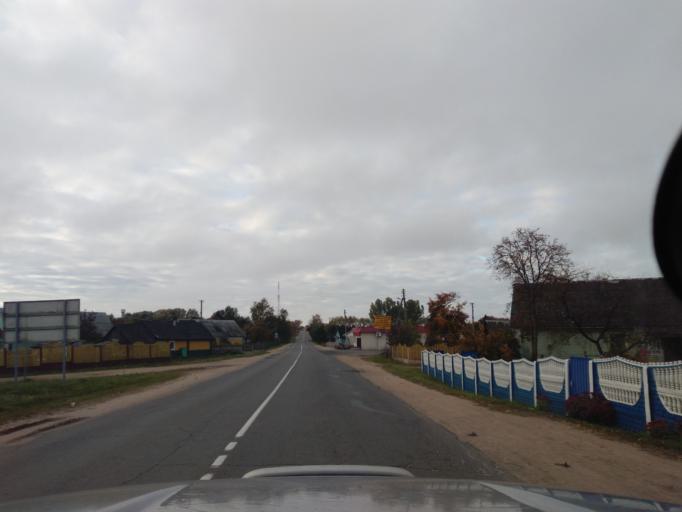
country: BY
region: Minsk
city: Kapyl'
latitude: 53.1588
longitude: 27.0779
